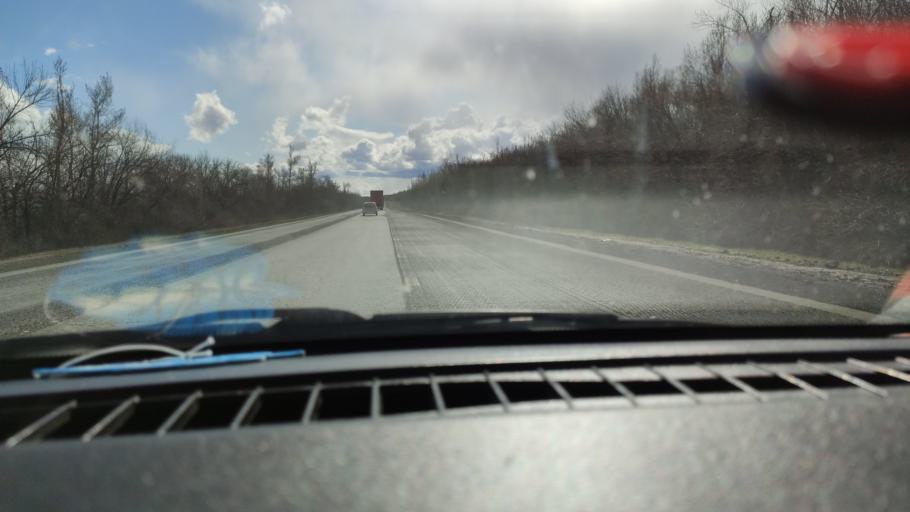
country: RU
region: Saratov
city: Dukhovnitskoye
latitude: 52.6566
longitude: 48.2062
